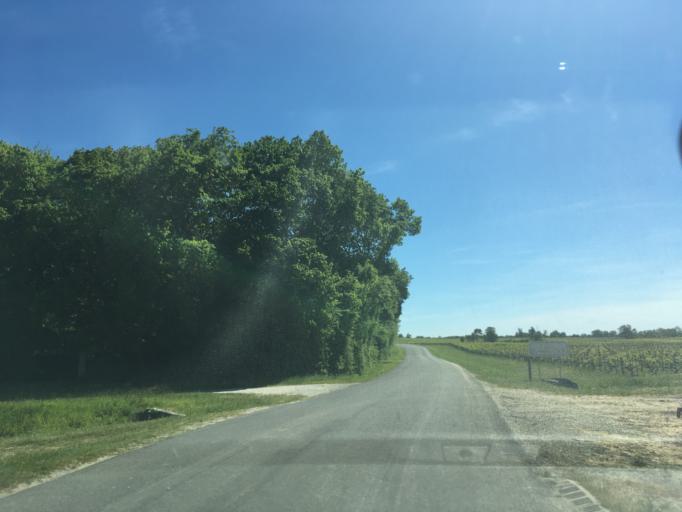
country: FR
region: Aquitaine
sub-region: Departement de la Gironde
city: Lesparre-Medoc
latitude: 45.3172
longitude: -0.8809
